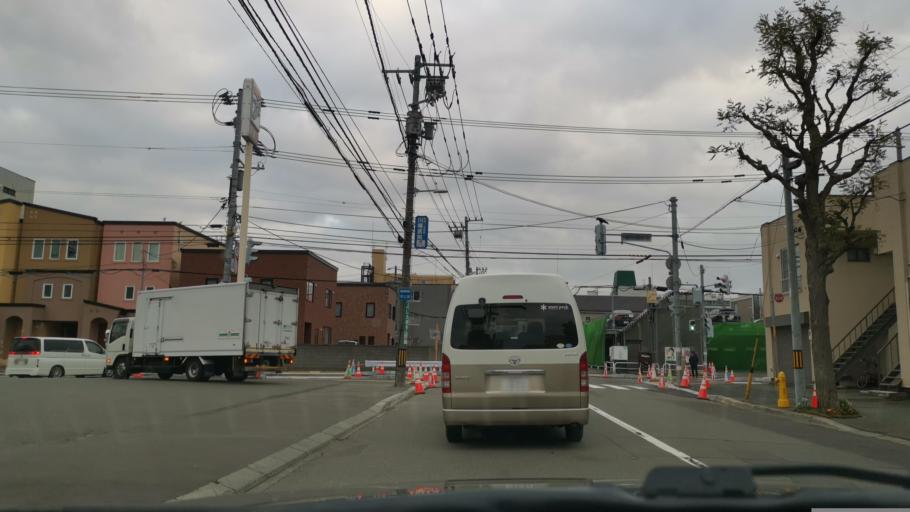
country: JP
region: Hokkaido
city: Sapporo
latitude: 43.0503
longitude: 141.3930
